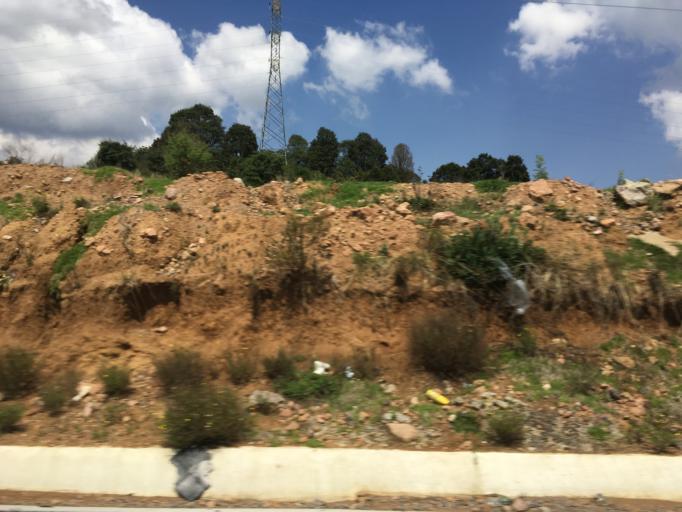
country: MX
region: Mexico
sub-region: Morelos
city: San Marcos Tlazalpan
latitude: 19.7888
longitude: -99.7029
